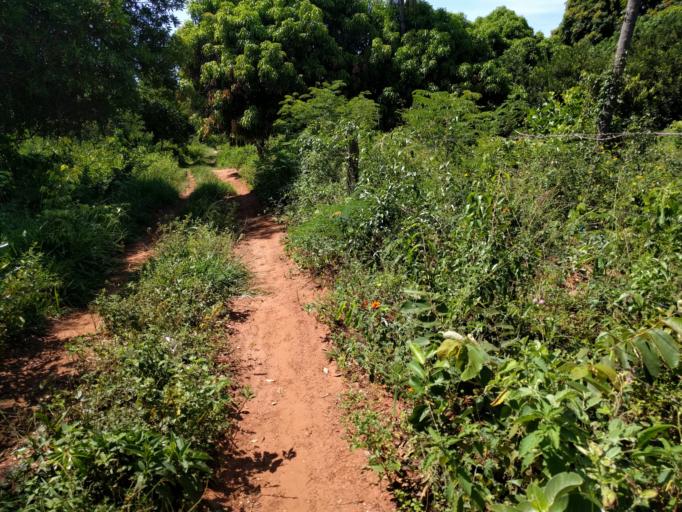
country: BO
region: Santa Cruz
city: Robore
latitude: -18.3366
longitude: -59.5980
